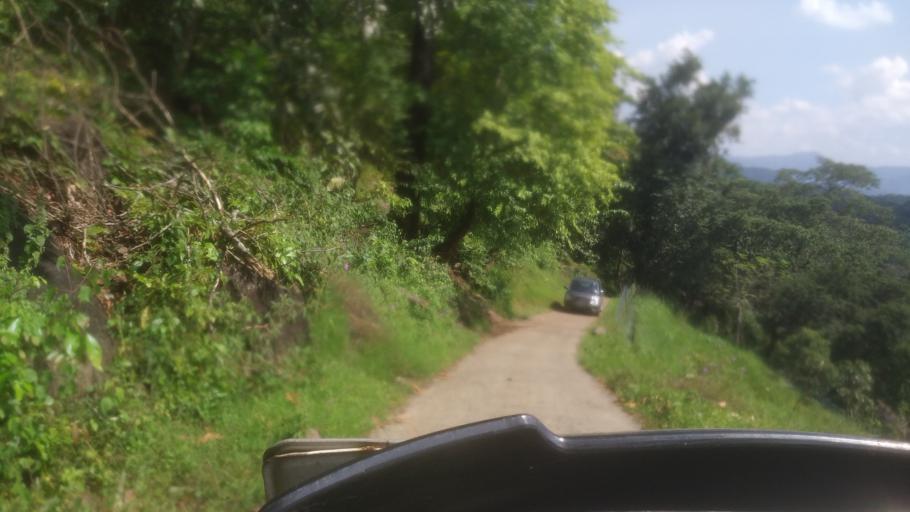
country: IN
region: Kerala
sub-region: Idukki
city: Idukki
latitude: 9.9633
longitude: 76.8243
